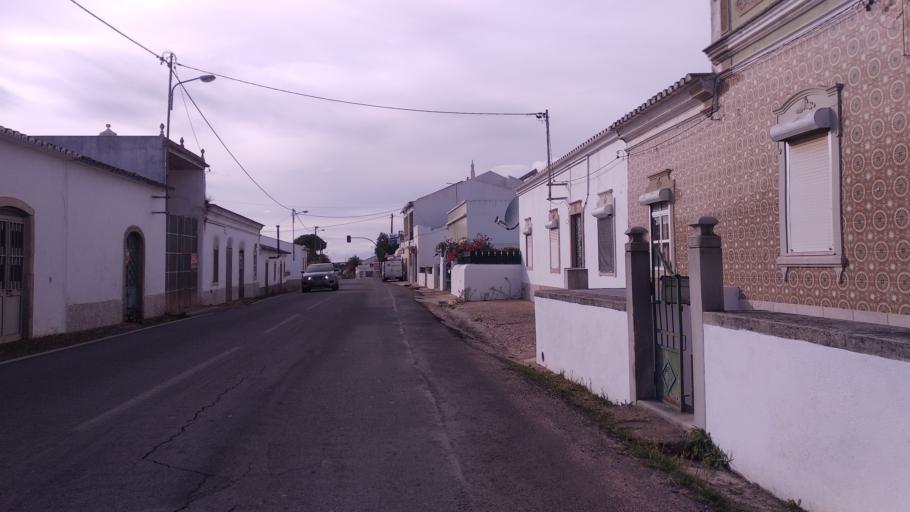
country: PT
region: Faro
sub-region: Sao Bras de Alportel
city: Sao Bras de Alportel
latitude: 37.1523
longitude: -7.9185
